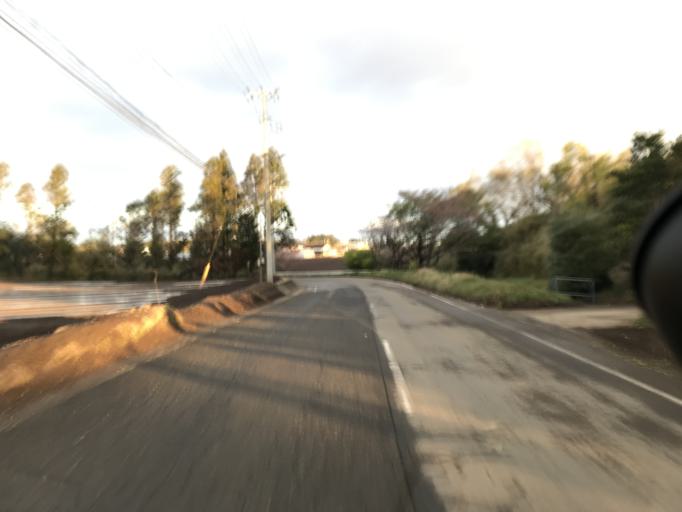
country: JP
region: Chiba
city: Sawara
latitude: 35.8286
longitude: 140.4621
